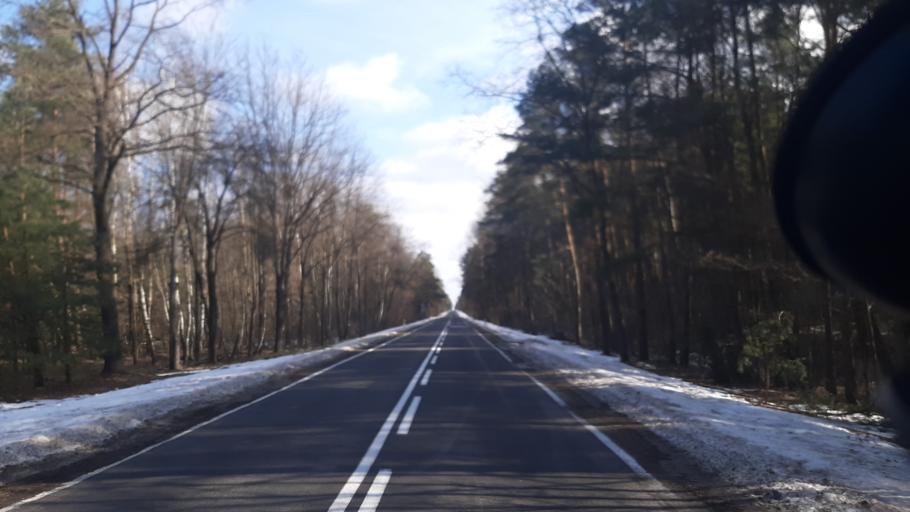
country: PL
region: Lublin Voivodeship
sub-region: Powiat parczewski
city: Sosnowica
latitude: 51.5117
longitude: 23.1064
